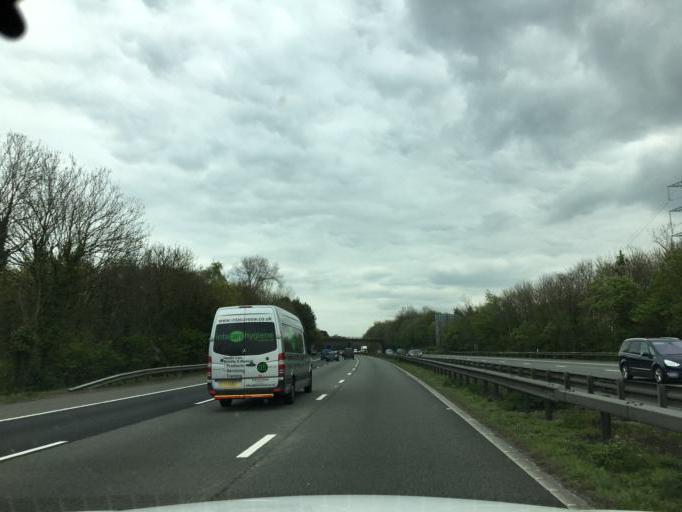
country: GB
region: Wales
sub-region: Cardiff
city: Pentyrch
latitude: 51.5099
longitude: -3.2997
